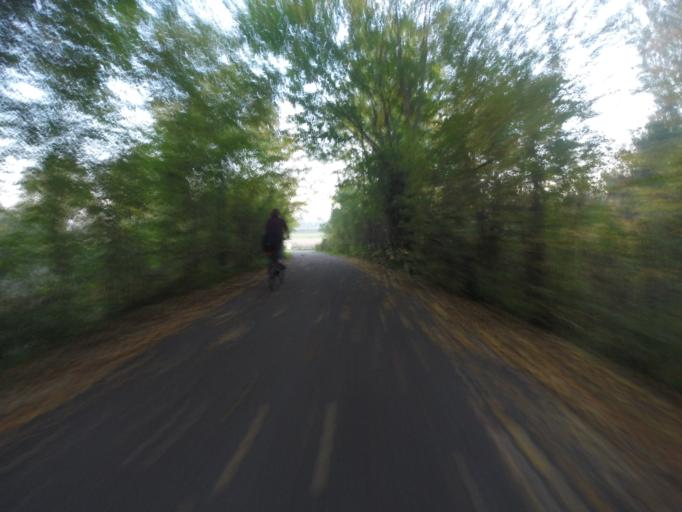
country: DK
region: Capital Region
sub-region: Hoje-Taastrup Kommune
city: Taastrup
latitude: 55.6595
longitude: 12.3231
